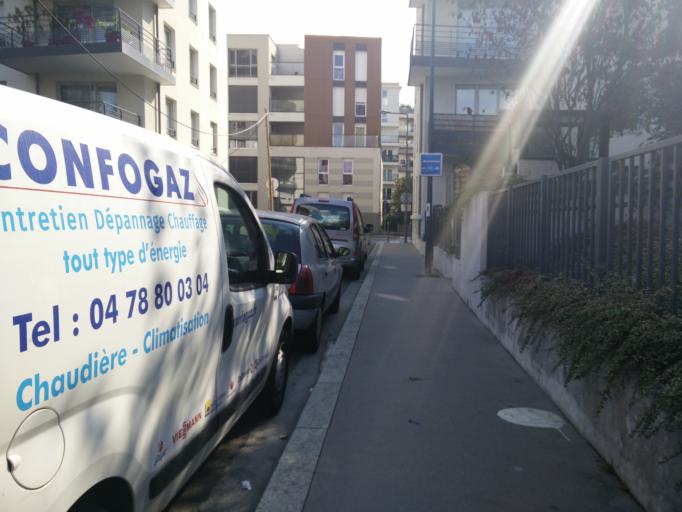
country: FR
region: Rhone-Alpes
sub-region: Departement du Rhone
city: Villeurbanne
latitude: 45.7566
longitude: 4.8893
